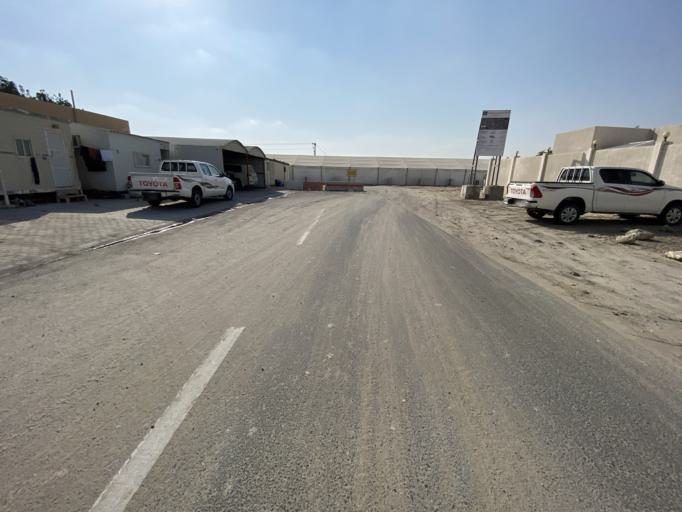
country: QA
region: Baladiyat ar Rayyan
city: Ar Rayyan
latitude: 25.2323
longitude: 51.3760
